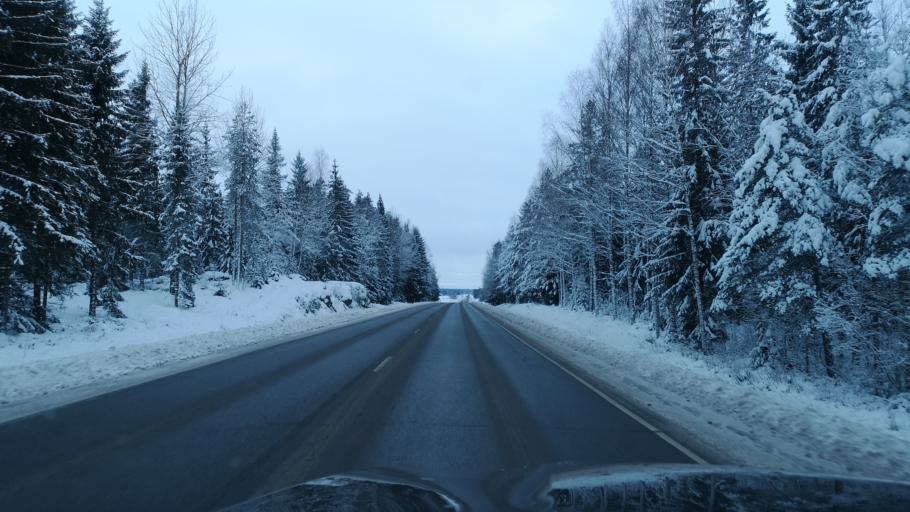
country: FI
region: Varsinais-Suomi
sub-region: Loimaa
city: Loimaa
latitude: 60.9001
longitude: 23.1359
